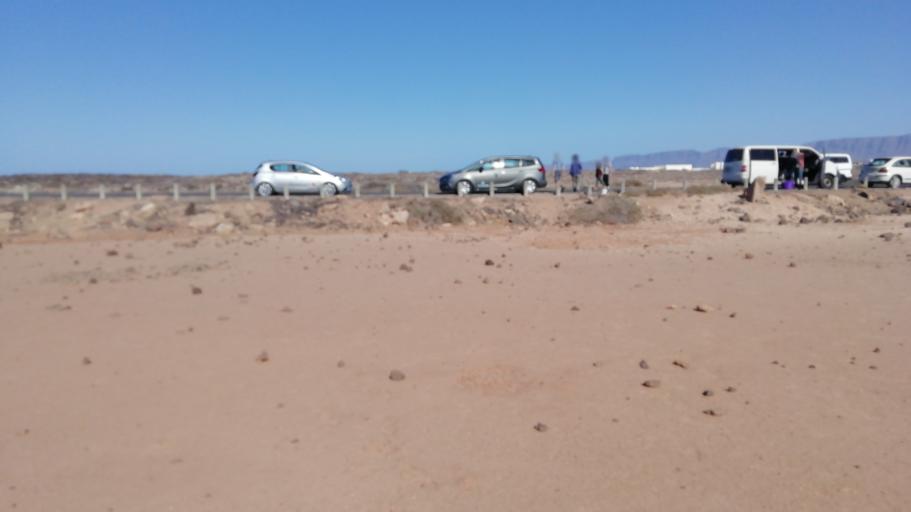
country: ES
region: Canary Islands
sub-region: Provincia de Las Palmas
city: Tinajo
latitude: 29.1168
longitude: -13.6609
